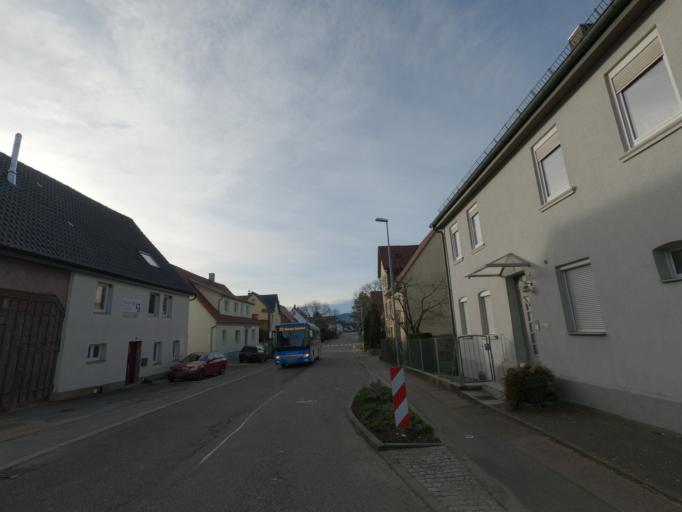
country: DE
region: Baden-Wuerttemberg
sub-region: Regierungsbezirk Stuttgart
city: Albershausen
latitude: 48.6868
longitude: 9.5823
